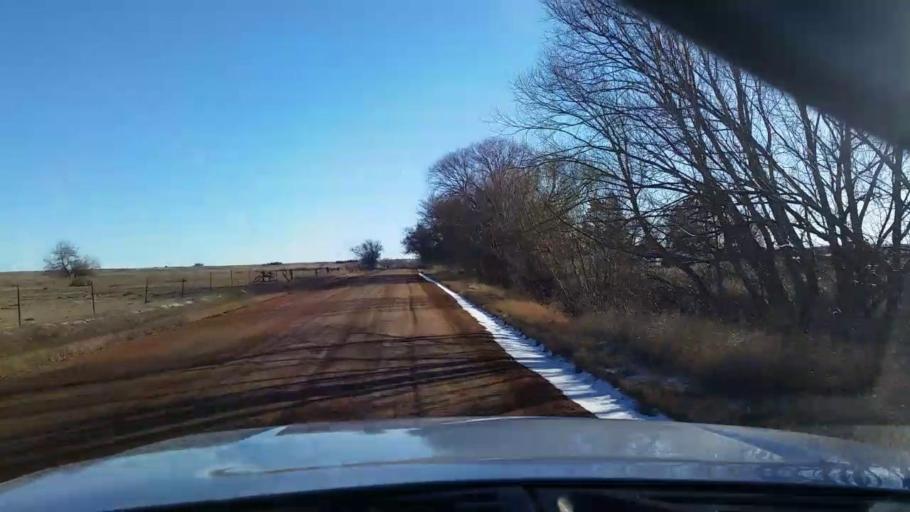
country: US
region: Colorado
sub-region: Larimer County
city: Wellington
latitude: 40.7694
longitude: -105.0501
